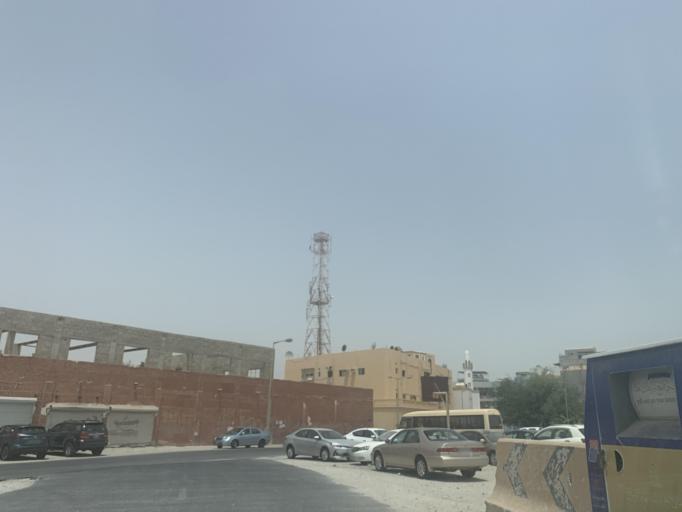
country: BH
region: Manama
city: Jidd Hafs
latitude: 26.2086
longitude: 50.5452
